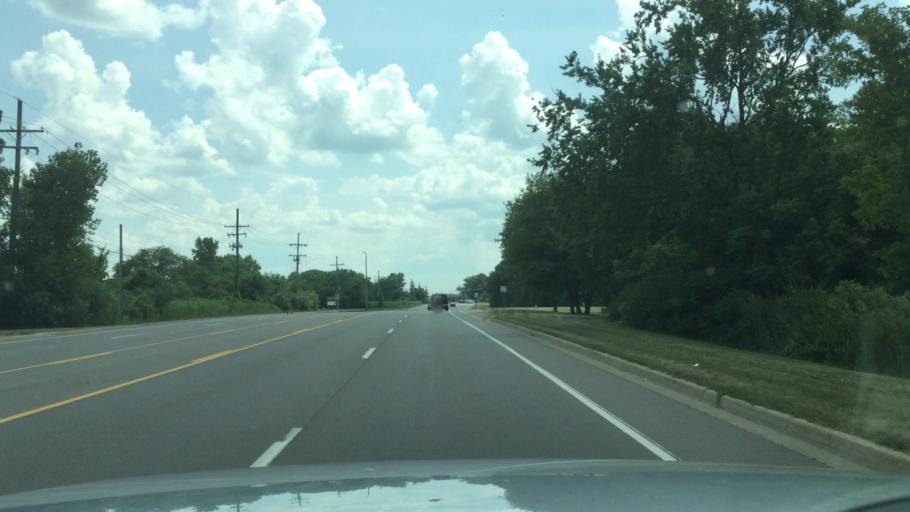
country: US
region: Michigan
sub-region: Washtenaw County
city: Ypsilanti
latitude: 42.2215
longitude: -83.6183
